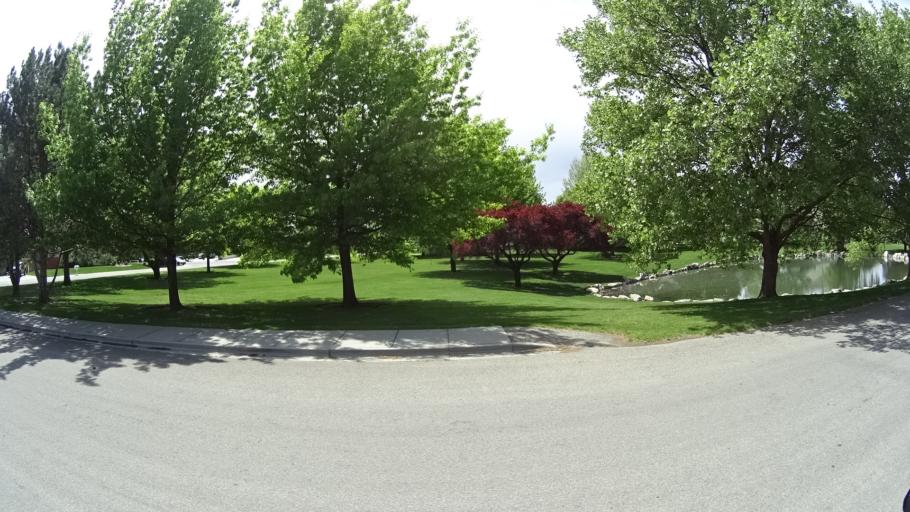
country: US
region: Idaho
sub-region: Ada County
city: Meridian
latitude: 43.5738
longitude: -116.4044
